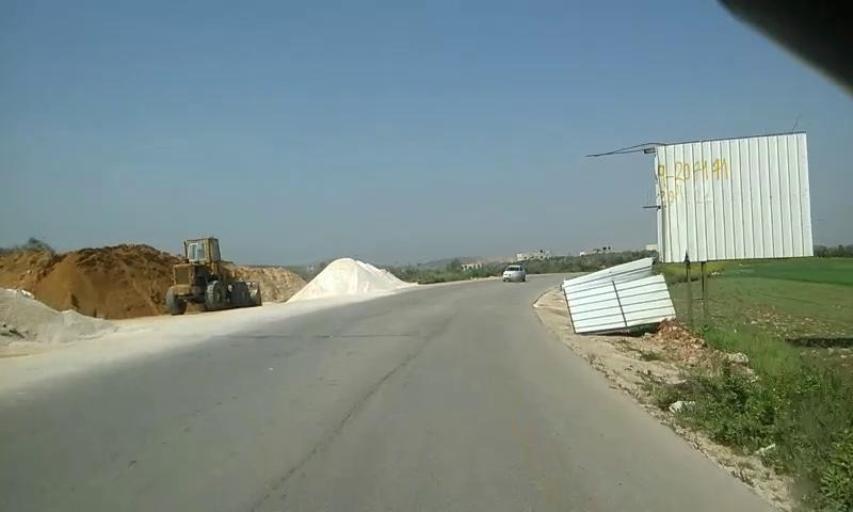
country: PS
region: West Bank
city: Az Zababidah
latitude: 32.3784
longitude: 35.3321
